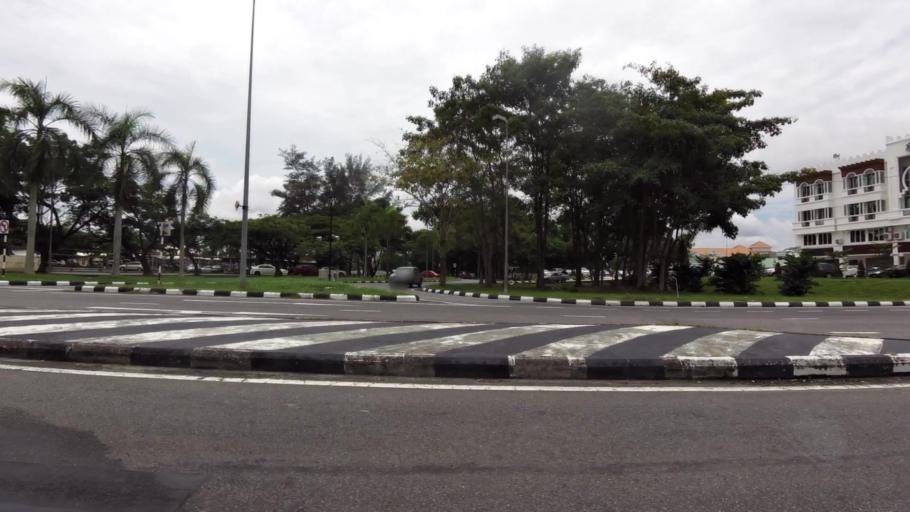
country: BN
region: Brunei and Muara
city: Bandar Seri Begawan
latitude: 4.9025
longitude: 114.9179
